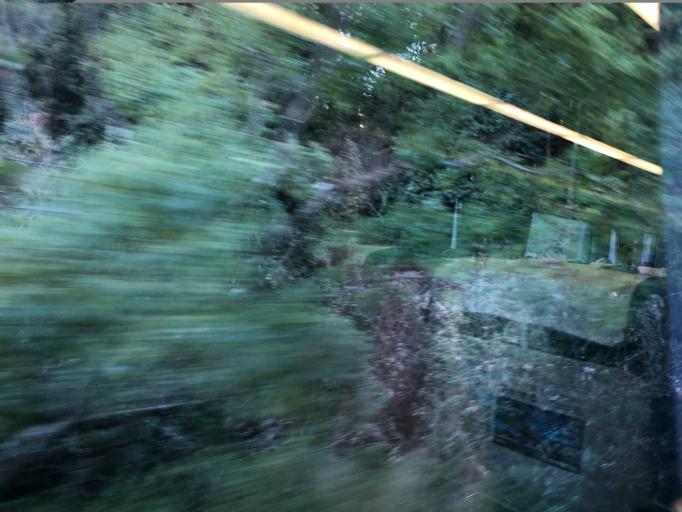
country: JP
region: Kochi
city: Nakamura
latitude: 33.0399
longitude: 133.0696
